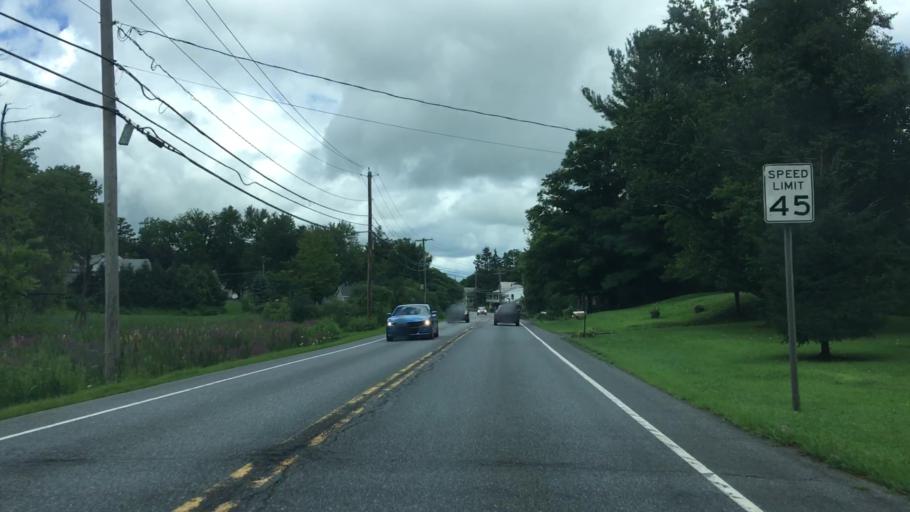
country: US
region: New York
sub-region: Rensselaer County
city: Poestenkill
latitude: 42.8102
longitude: -73.5392
